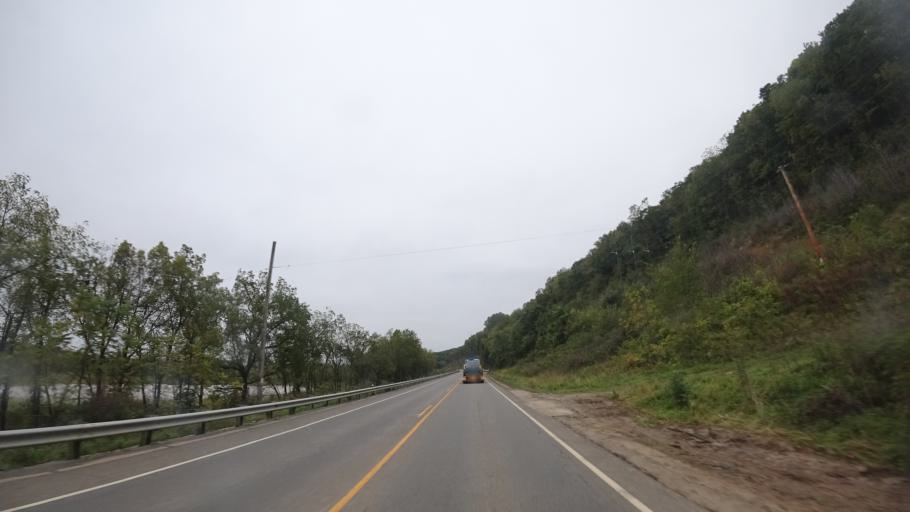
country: US
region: Wisconsin
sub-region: Crawford County
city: Prairie du Chien
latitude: 43.0720
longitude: -90.9414
